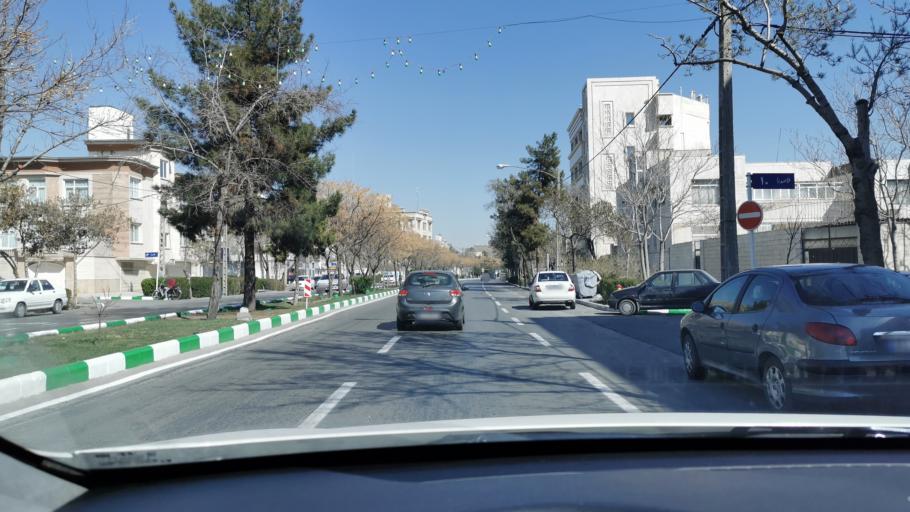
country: IR
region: Razavi Khorasan
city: Mashhad
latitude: 36.2925
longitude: 59.5722
